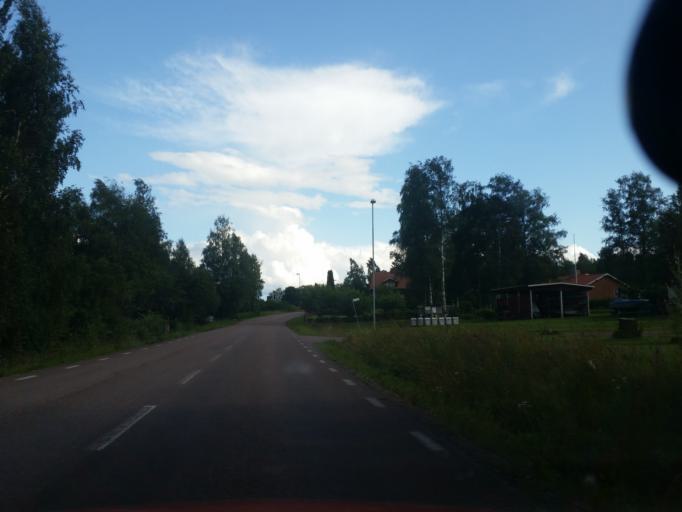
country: SE
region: Dalarna
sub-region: Leksand Municipality
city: Smedby
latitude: 60.6773
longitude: 15.1271
